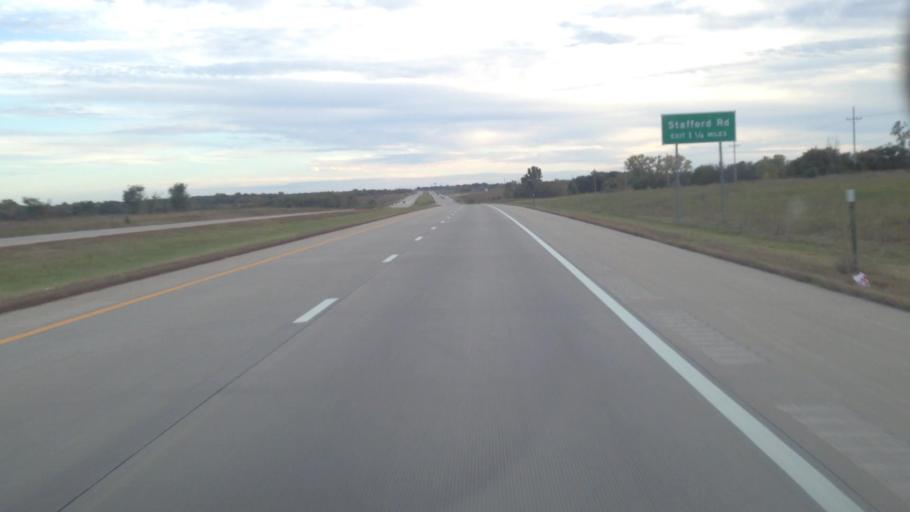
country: US
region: Kansas
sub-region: Douglas County
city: Baldwin City
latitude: 38.7312
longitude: -95.2685
